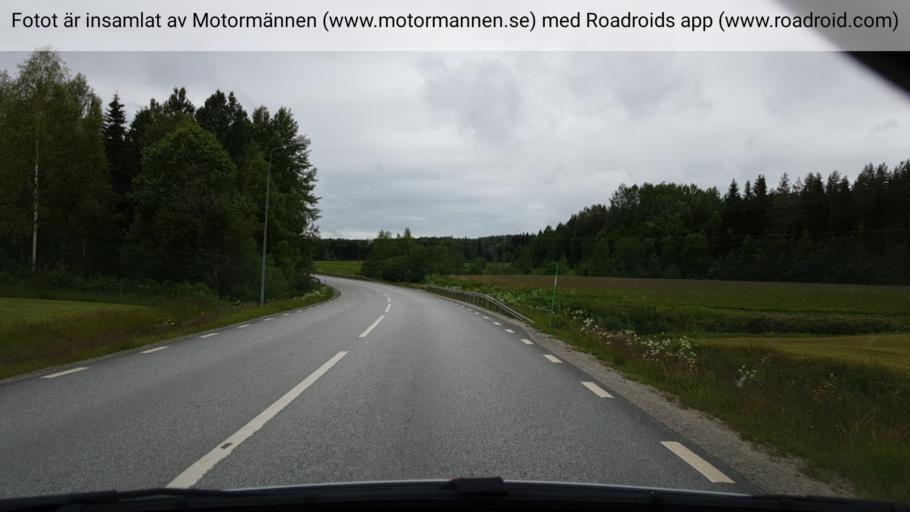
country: SE
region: Vaesterbotten
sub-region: Vindelns Kommun
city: Vindeln
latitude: 64.1219
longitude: 19.5610
